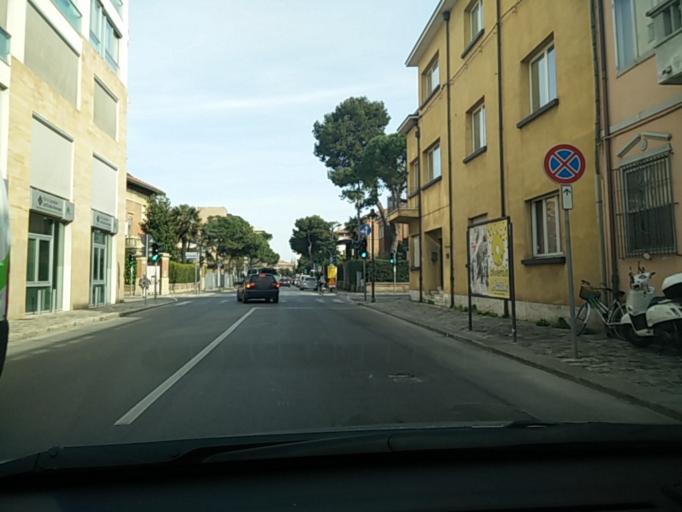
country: IT
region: Emilia-Romagna
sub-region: Provincia di Rimini
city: Rimini
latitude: 44.0639
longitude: 12.5697
